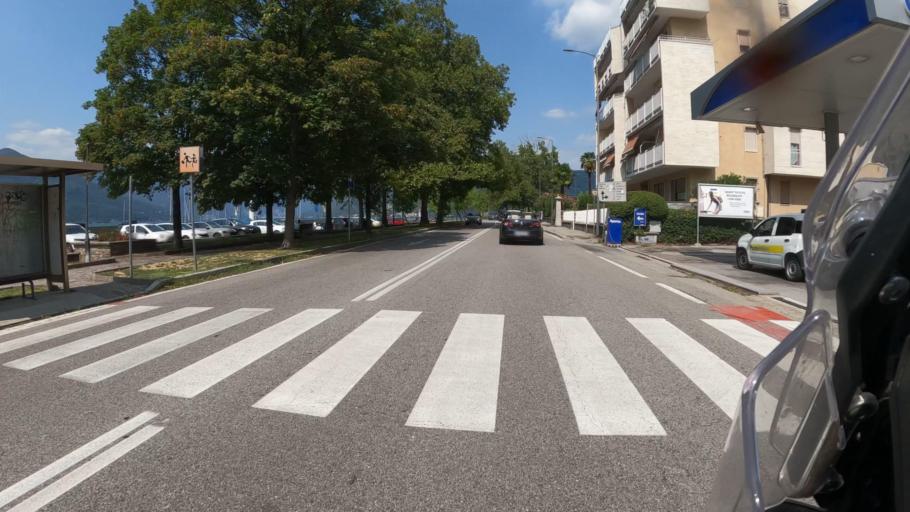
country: IT
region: Lombardy
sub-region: Provincia di Varese
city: Luino
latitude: 45.9981
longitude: 8.7347
